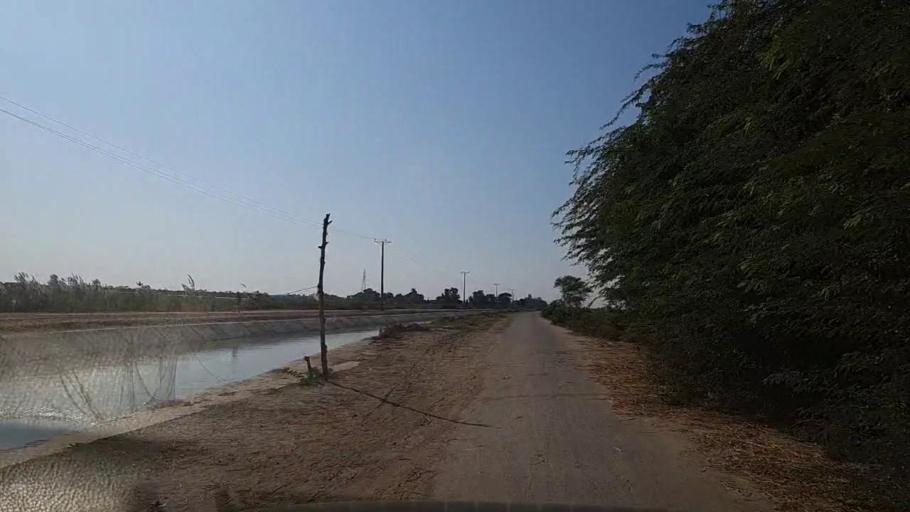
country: PK
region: Sindh
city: Thatta
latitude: 24.5962
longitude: 67.8197
